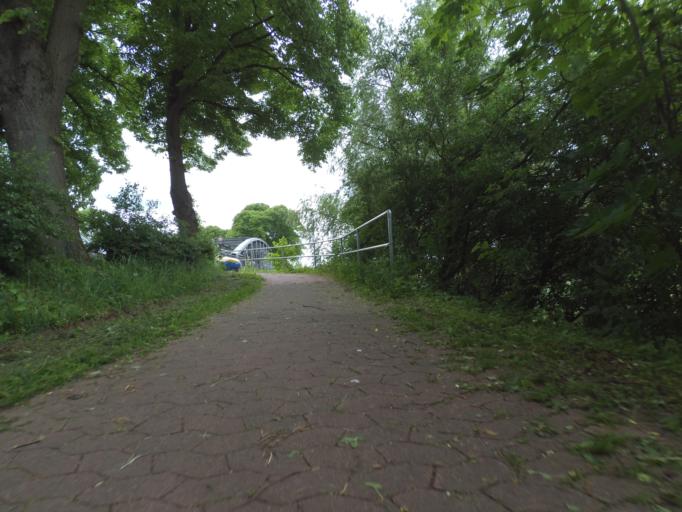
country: DE
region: Lower Saxony
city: Wunstorf
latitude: 52.4261
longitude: 9.5000
